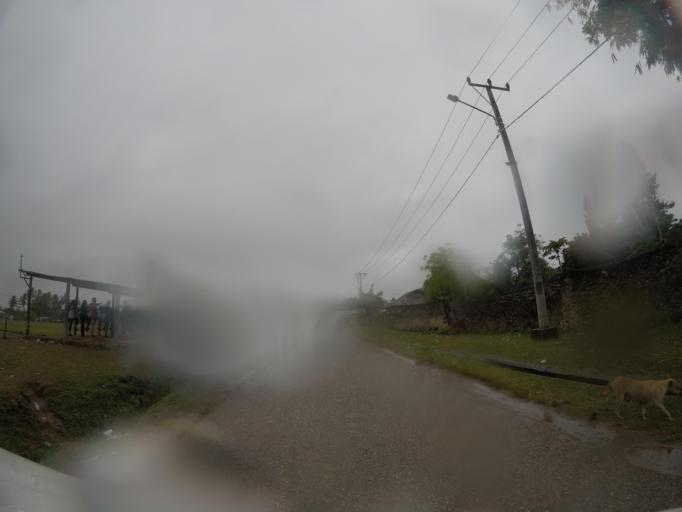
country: TL
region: Lautem
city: Lospalos
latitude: -8.5213
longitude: 126.9977
